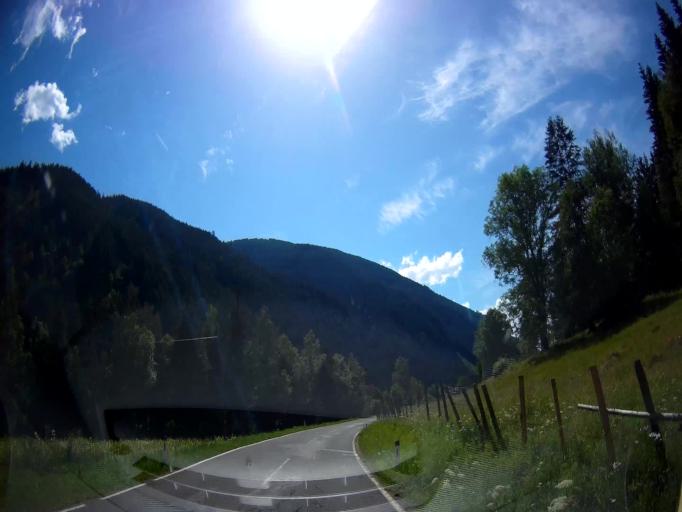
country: AT
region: Salzburg
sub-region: Politischer Bezirk Tamsweg
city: Thomatal
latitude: 47.0643
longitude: 13.7721
